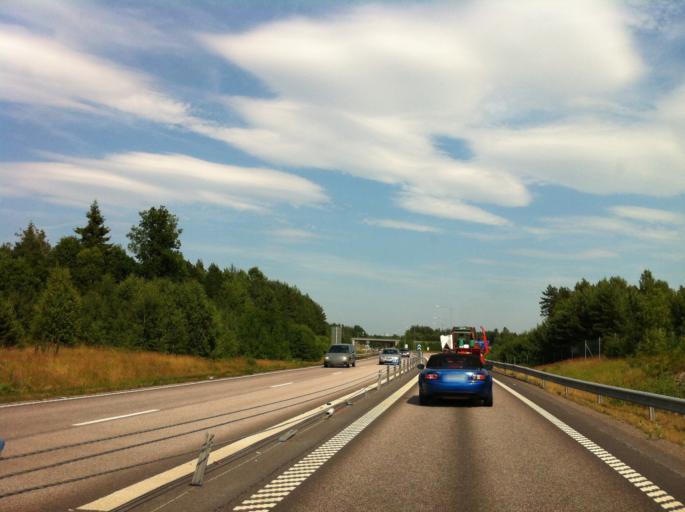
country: SE
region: Kalmar
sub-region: Kalmar Kommun
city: Trekanten
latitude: 56.6898
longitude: 16.1141
